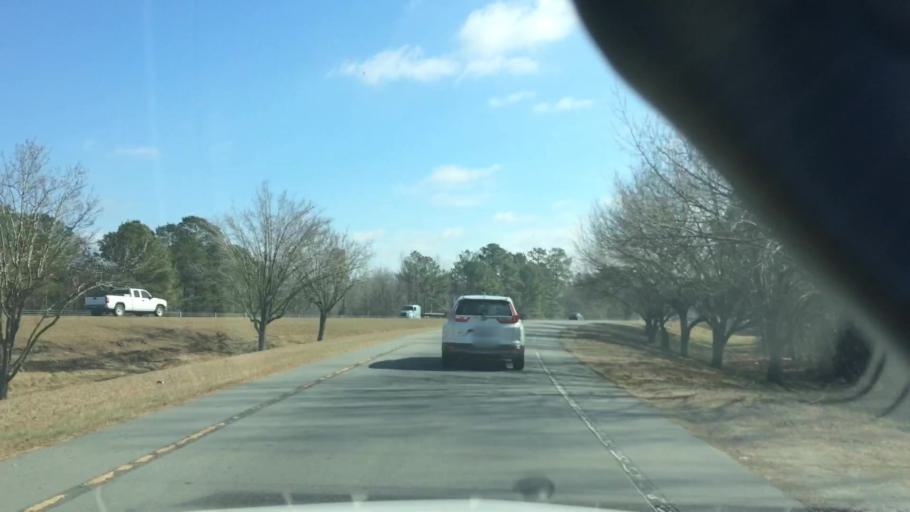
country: US
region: North Carolina
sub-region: Duplin County
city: Wallace
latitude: 34.7531
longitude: -77.9494
